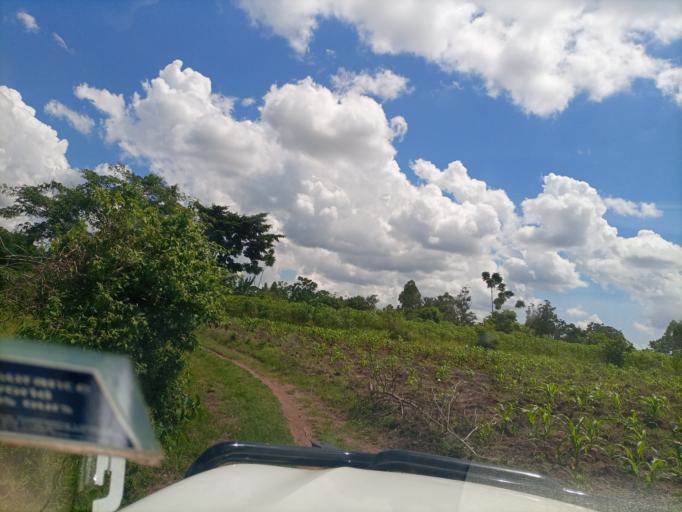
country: UG
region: Eastern Region
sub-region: Tororo District
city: Tororo
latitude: 0.7213
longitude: 34.0228
